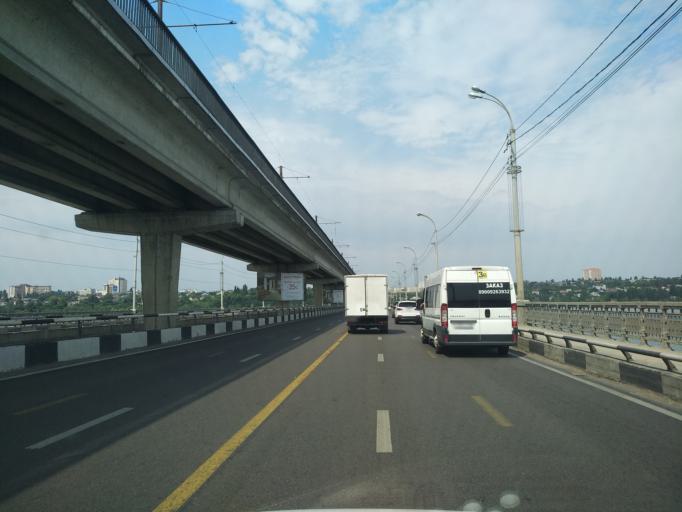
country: RU
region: Voronezj
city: Voronezh
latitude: 51.6905
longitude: 39.2453
